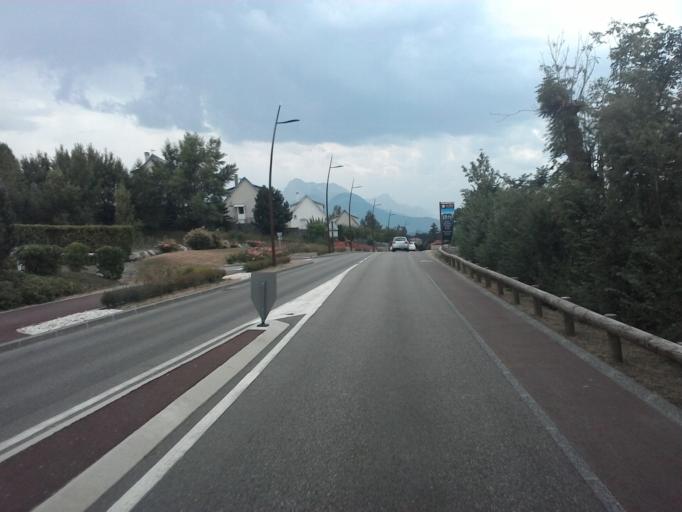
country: FR
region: Rhone-Alpes
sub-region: Departement de l'Isere
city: La Mure
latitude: 44.9164
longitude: 5.7844
